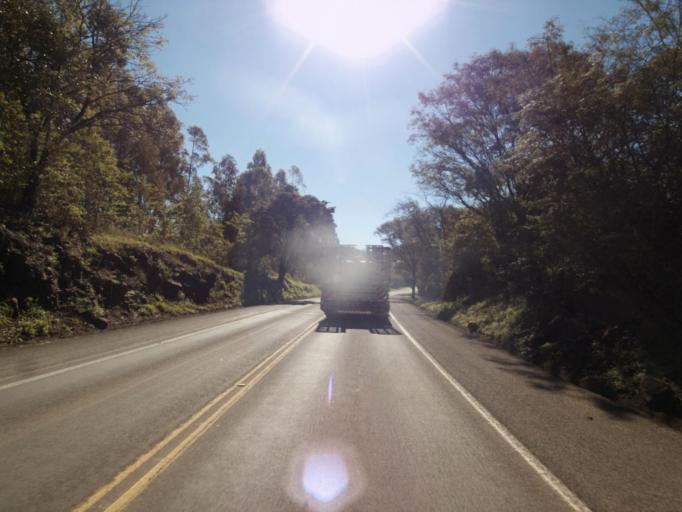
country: BR
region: Rio Grande do Sul
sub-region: Frederico Westphalen
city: Frederico Westphalen
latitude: -26.7985
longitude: -53.4494
